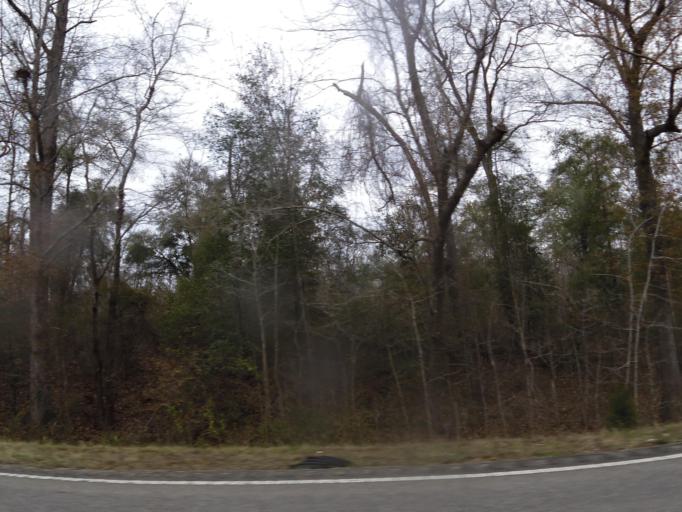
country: US
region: Alabama
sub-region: Barbour County
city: Eufaula
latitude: 31.9359
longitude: -85.1694
